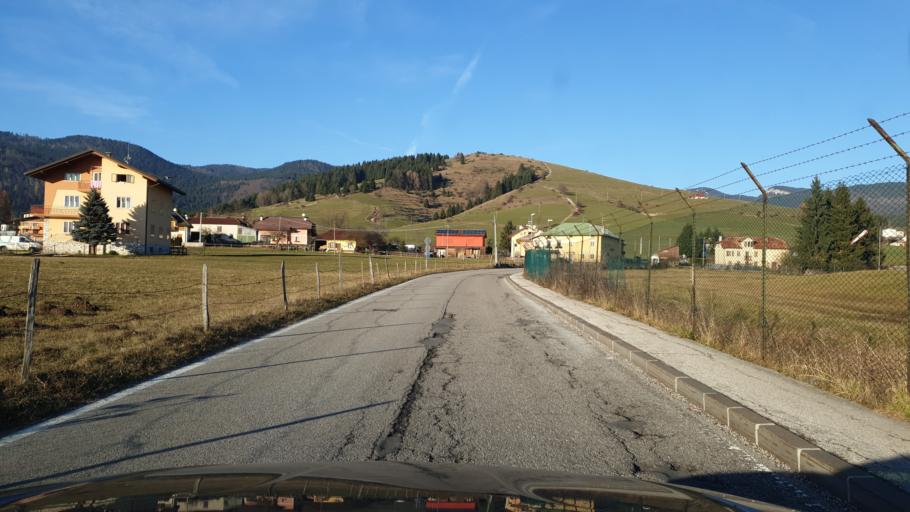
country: IT
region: Veneto
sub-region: Provincia di Vicenza
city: Asiago
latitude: 45.8848
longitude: 11.5081
